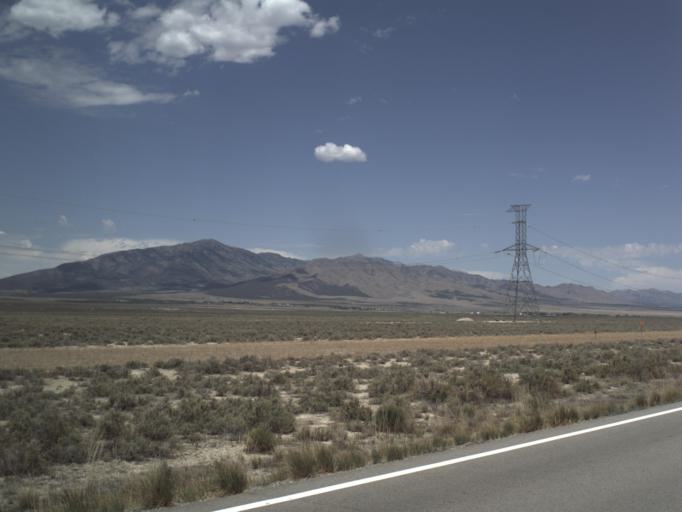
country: US
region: Utah
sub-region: Tooele County
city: Tooele
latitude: 40.2884
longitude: -112.4002
